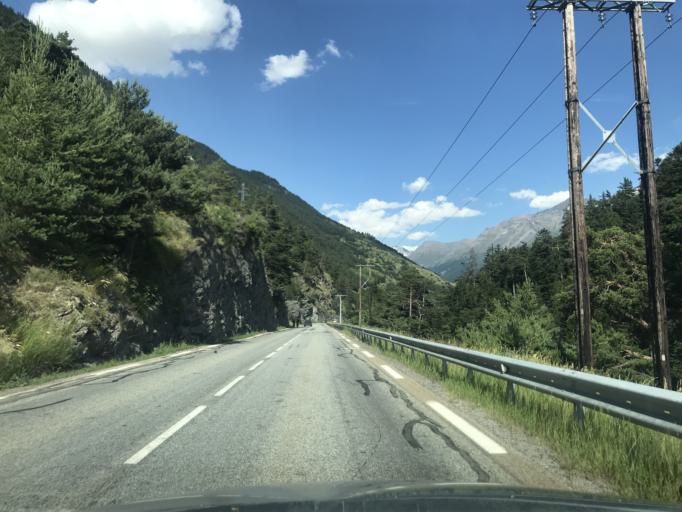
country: IT
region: Piedmont
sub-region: Provincia di Torino
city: Moncenisio
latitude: 45.2843
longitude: 6.8335
